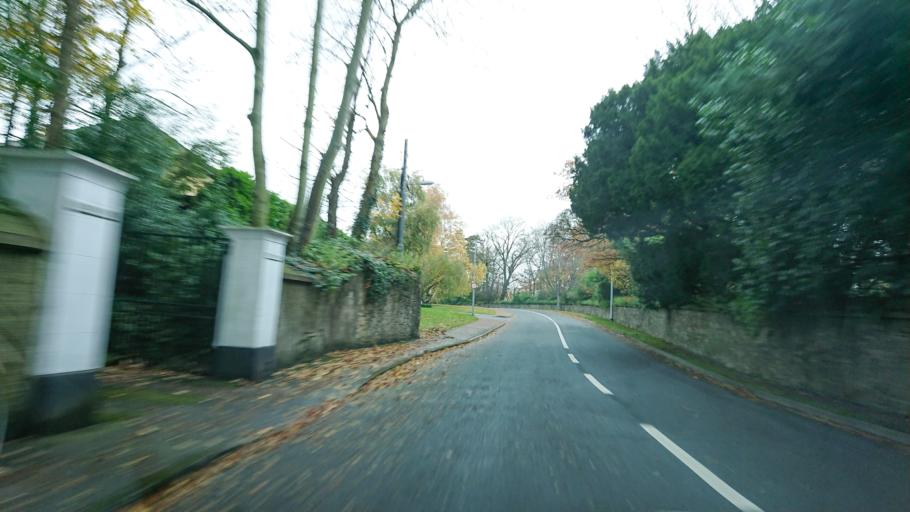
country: IE
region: Munster
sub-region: South Tipperary
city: Cluain Meala
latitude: 52.3518
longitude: -7.6898
